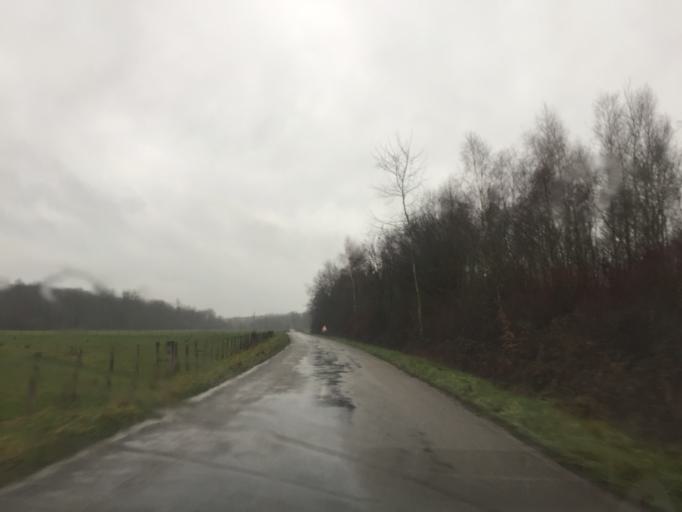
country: FR
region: Franche-Comte
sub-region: Departement du Doubs
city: Arc-et-Senans
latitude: 47.0042
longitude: 5.7715
